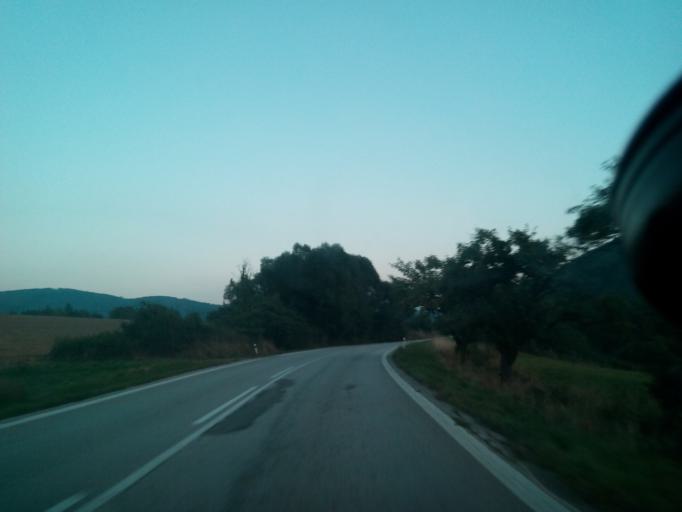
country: SK
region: Kosicky
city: Dobsina
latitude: 48.7796
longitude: 20.4079
